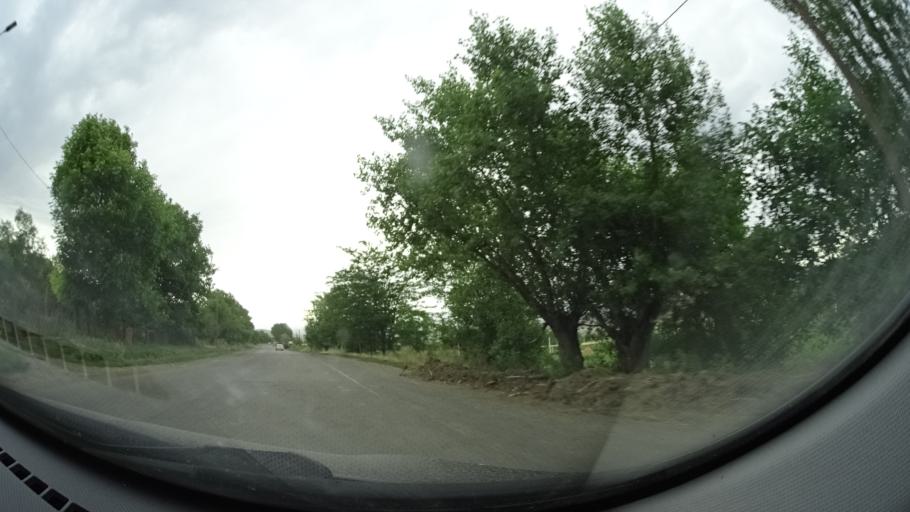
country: GE
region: Samtskhe-Javakheti
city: Akhaltsikhe
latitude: 41.6368
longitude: 43.0388
